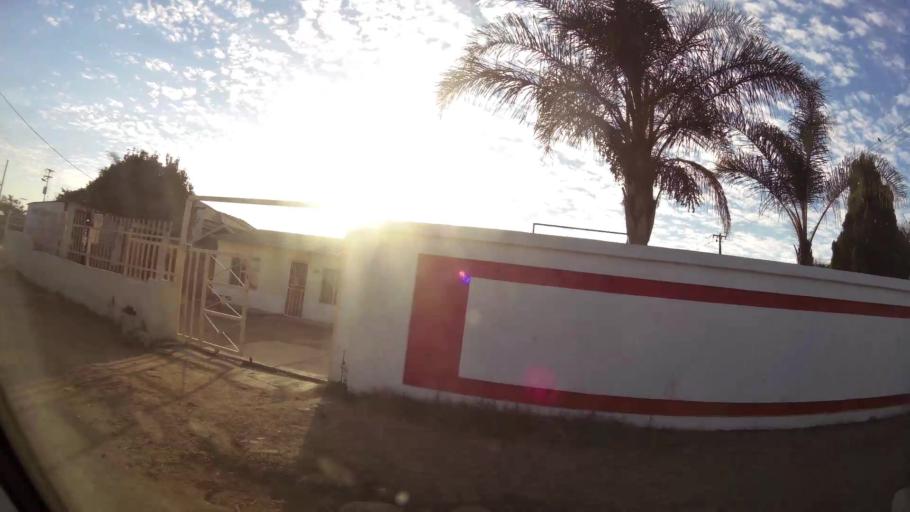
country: ZA
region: Gauteng
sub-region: City of Tshwane Metropolitan Municipality
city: Cullinan
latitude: -25.7075
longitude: 28.3856
